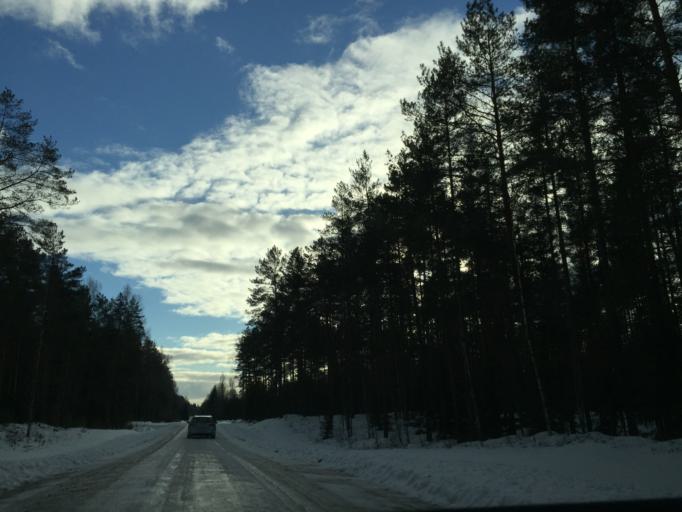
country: LV
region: Ogre
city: Jumprava
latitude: 56.5589
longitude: 24.8552
